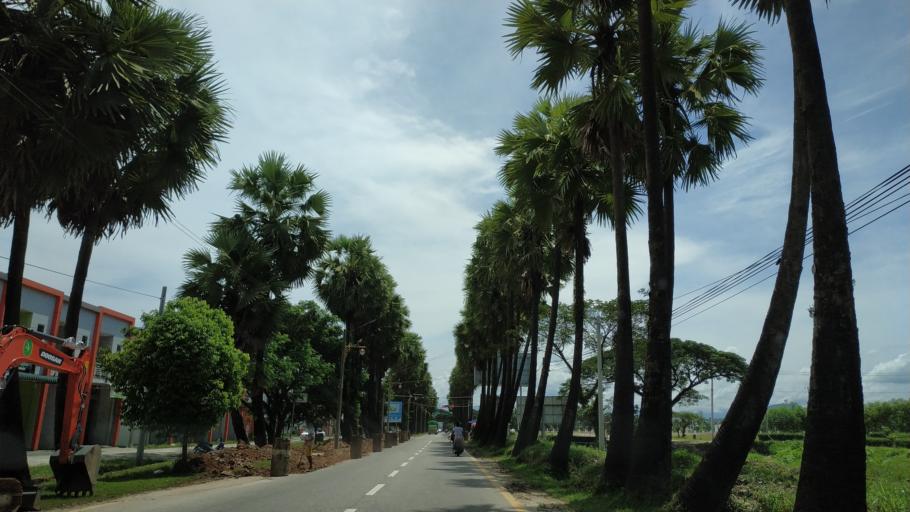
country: MM
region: Tanintharyi
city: Dawei
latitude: 14.0943
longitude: 98.1775
